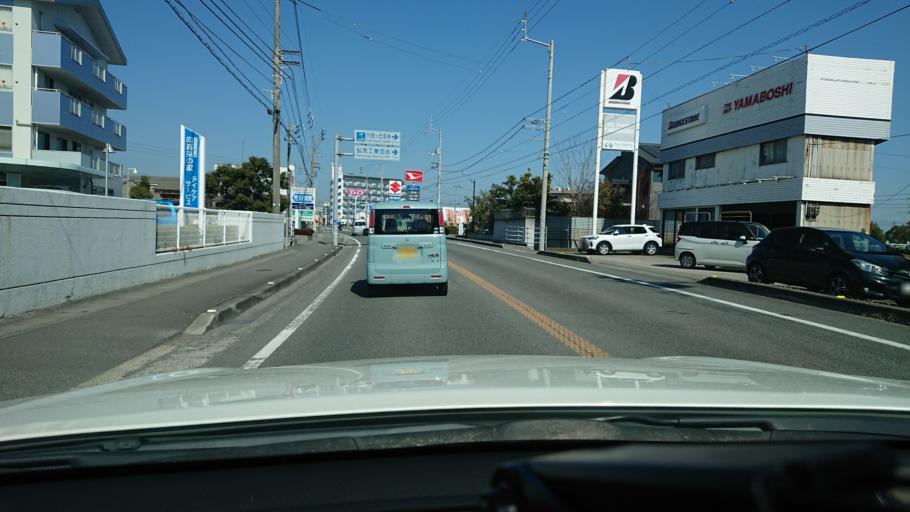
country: JP
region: Tokushima
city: Narutocho-mitsuishi
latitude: 34.1433
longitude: 134.5935
